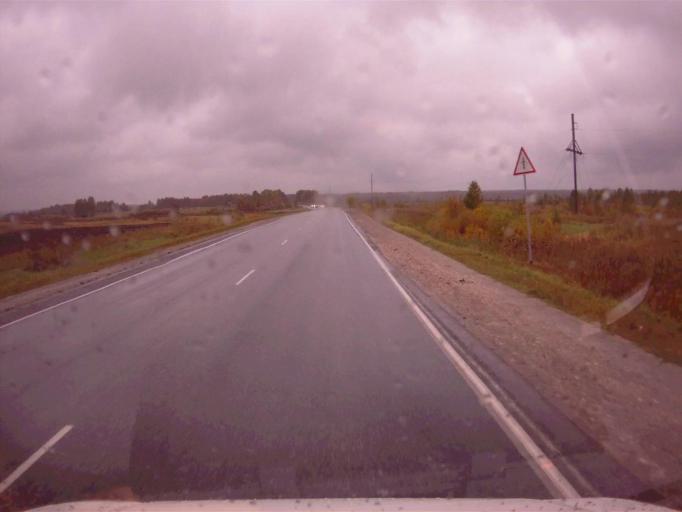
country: RU
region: Chelyabinsk
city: Argayash
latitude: 55.4792
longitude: 60.8150
